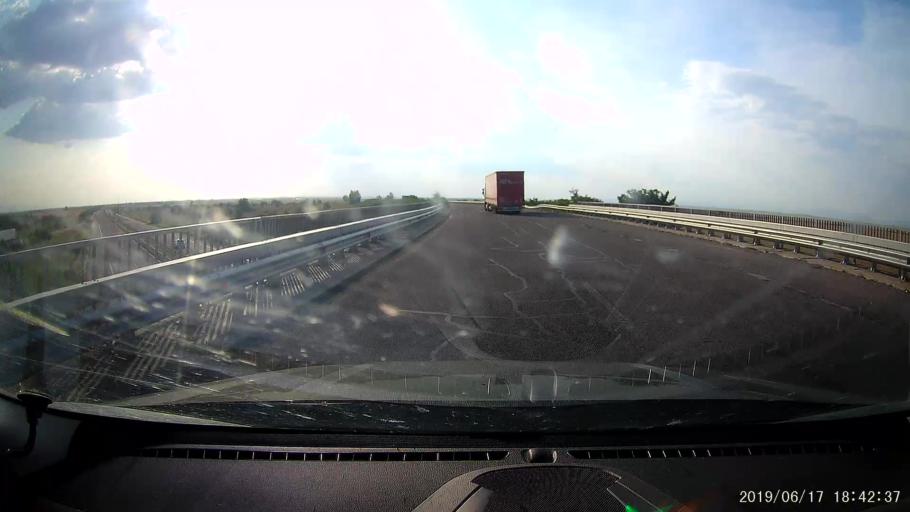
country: BG
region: Stara Zagora
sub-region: Obshtina Chirpan
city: Chirpan
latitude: 42.1941
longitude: 25.2341
